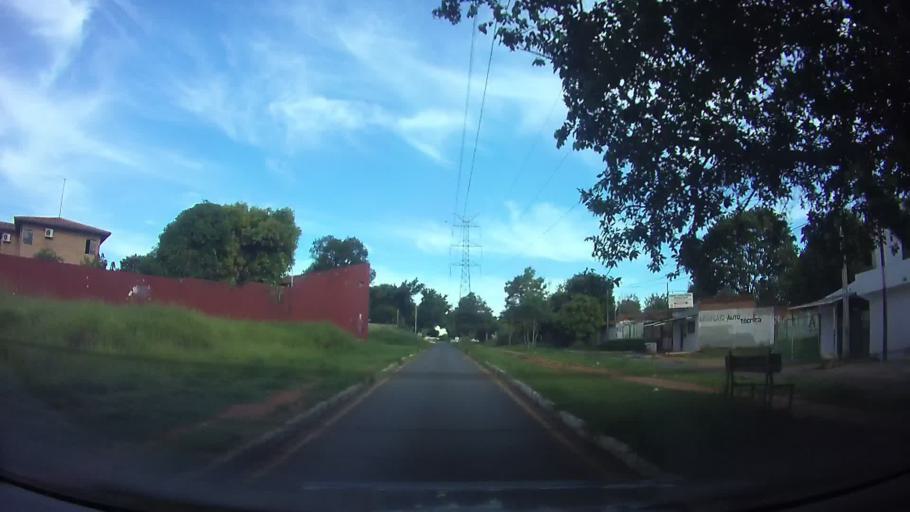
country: PY
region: Central
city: San Antonio
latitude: -25.4248
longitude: -57.5362
